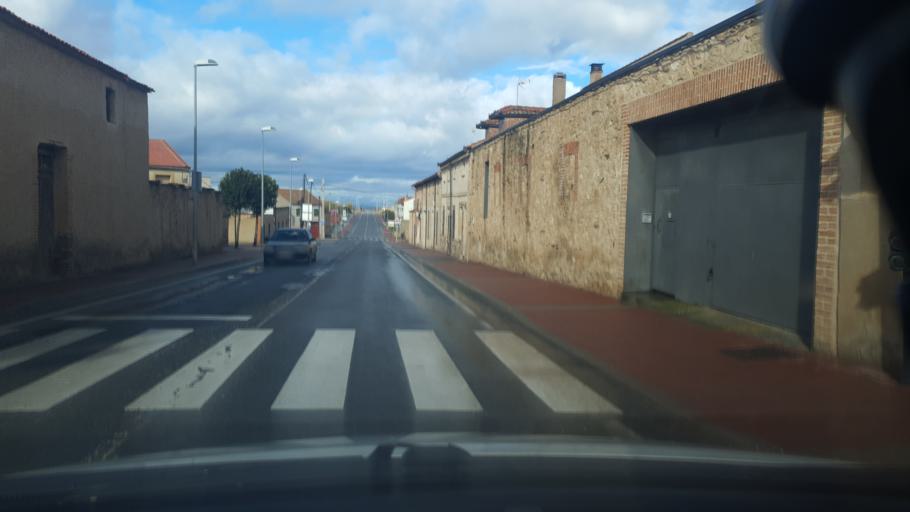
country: ES
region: Castille and Leon
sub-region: Provincia de Segovia
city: Carbonero el Mayor
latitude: 41.1232
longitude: -4.2684
